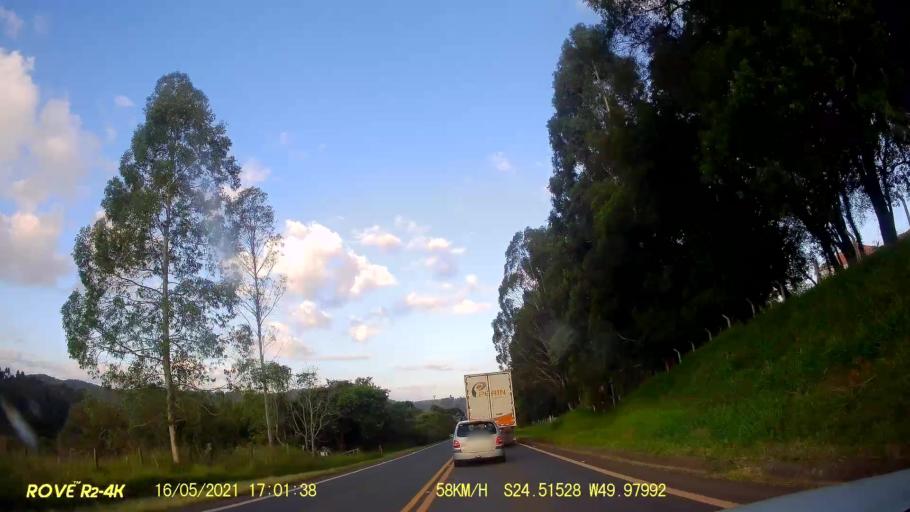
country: BR
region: Parana
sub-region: Pirai Do Sul
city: Pirai do Sul
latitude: -24.5153
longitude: -49.9799
